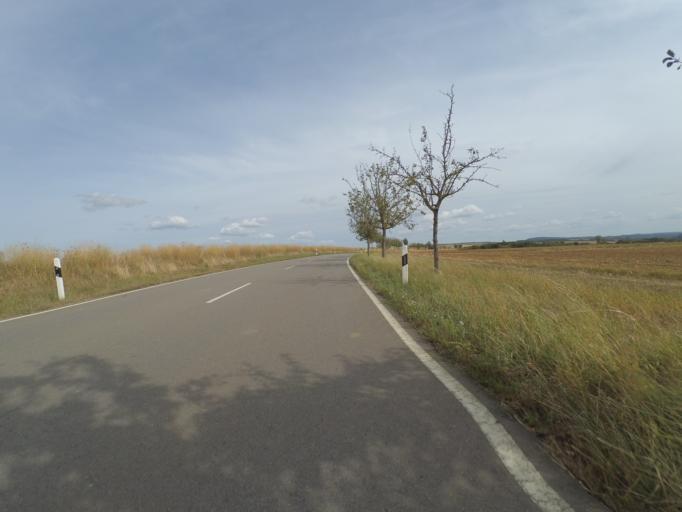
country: LU
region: Grevenmacher
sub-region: Canton de Remich
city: Mondorf-les-Bains
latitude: 49.4921
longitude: 6.3027
